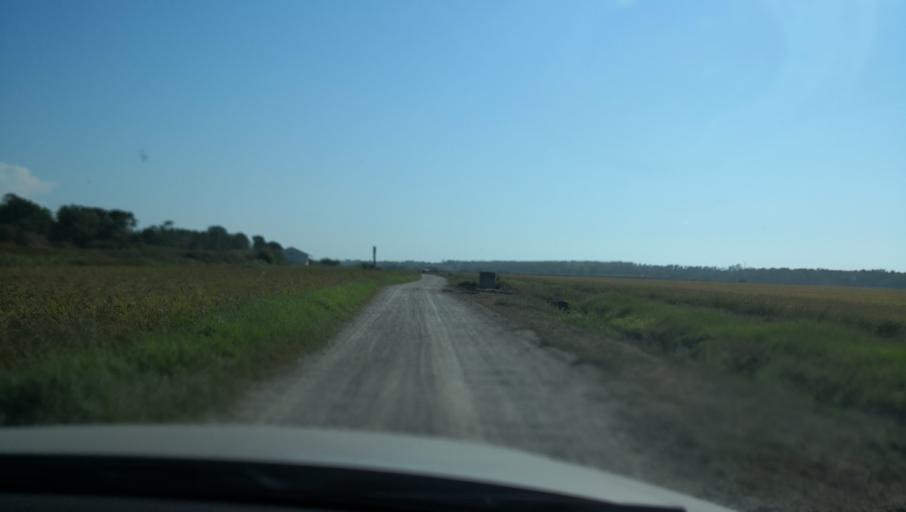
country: PT
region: Setubal
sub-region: Setubal
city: Setubal
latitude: 38.3923
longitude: -8.7892
